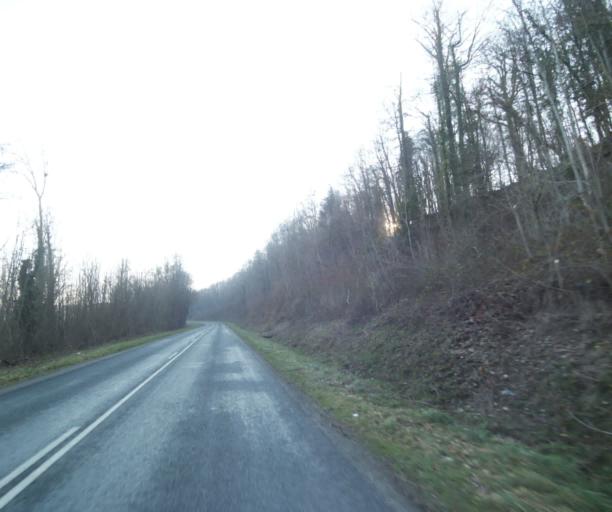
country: FR
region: Champagne-Ardenne
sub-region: Departement de la Haute-Marne
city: Bienville
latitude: 48.5733
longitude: 5.0377
